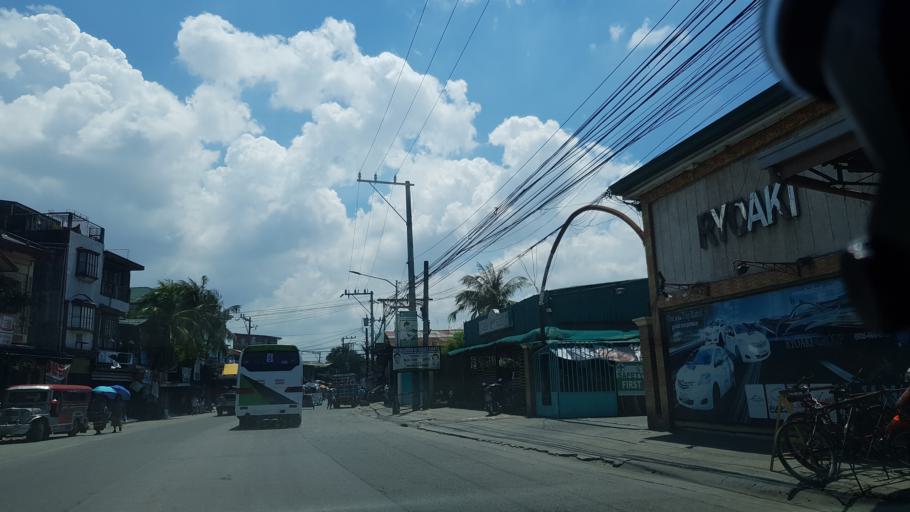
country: PH
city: Sambayanihan People's Village
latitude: 14.4727
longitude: 120.9989
